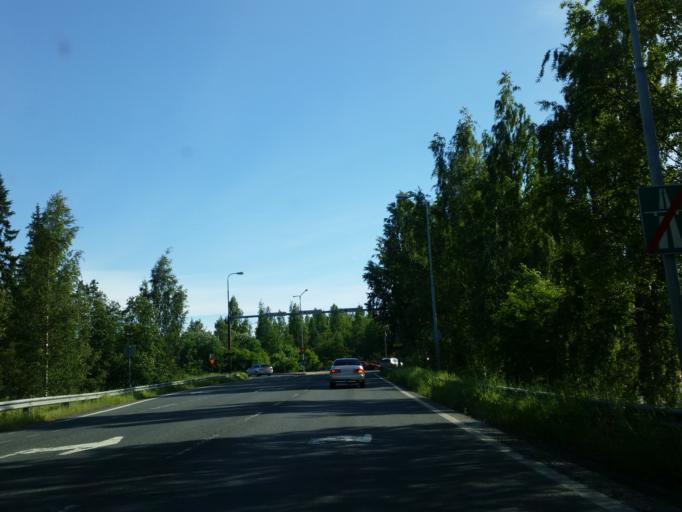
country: FI
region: Northern Savo
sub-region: Kuopio
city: Kuopio
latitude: 62.9067
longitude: 27.6853
